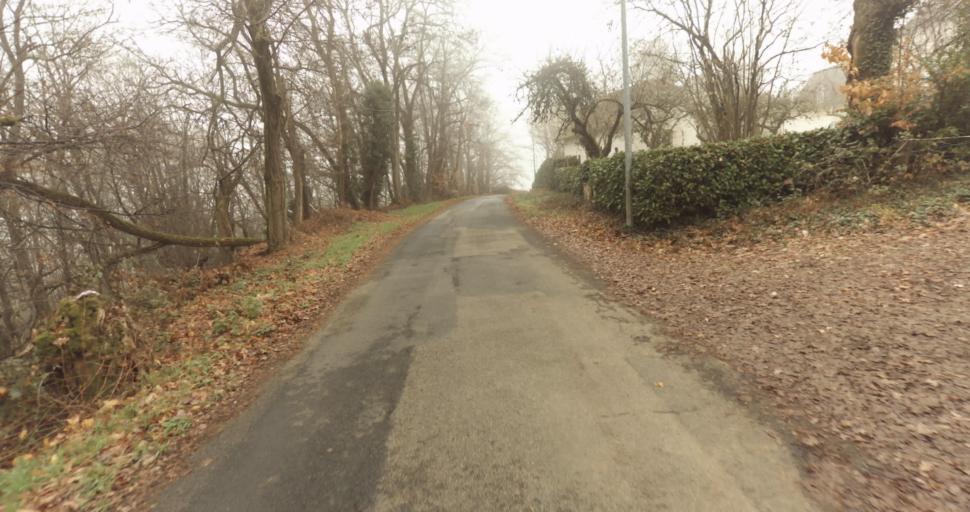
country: FR
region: Midi-Pyrenees
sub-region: Departement du Lot
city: Figeac
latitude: 44.6174
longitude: 2.0446
